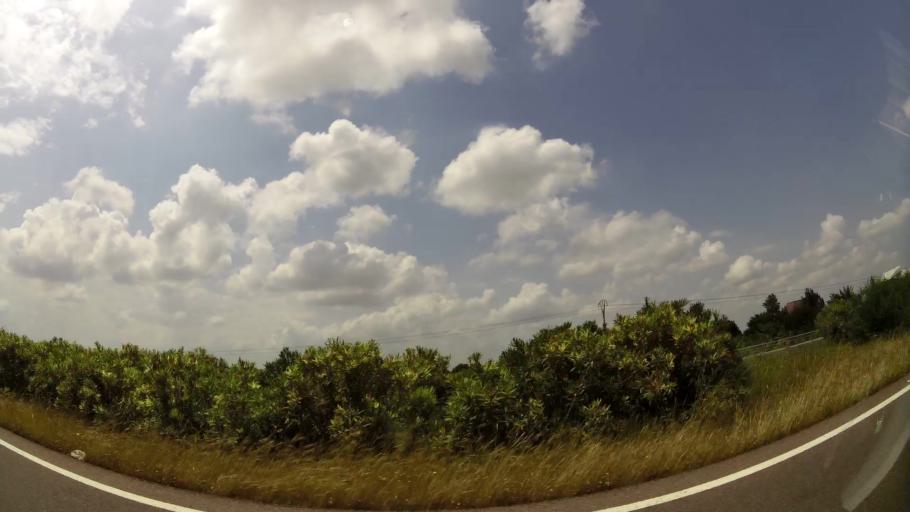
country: MA
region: Rabat-Sale-Zemmour-Zaer
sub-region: Khemisset
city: Tiflet
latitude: 33.9788
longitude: -6.5198
